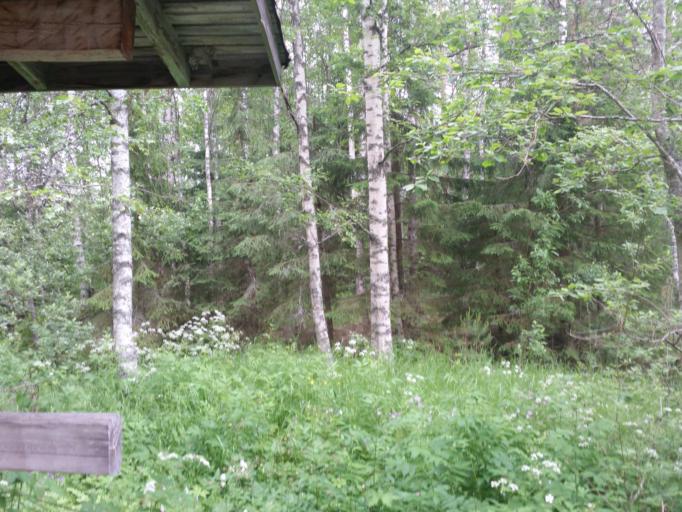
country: FI
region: Northern Savo
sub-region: Koillis-Savo
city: Kaavi
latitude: 62.9811
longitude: 28.7639
